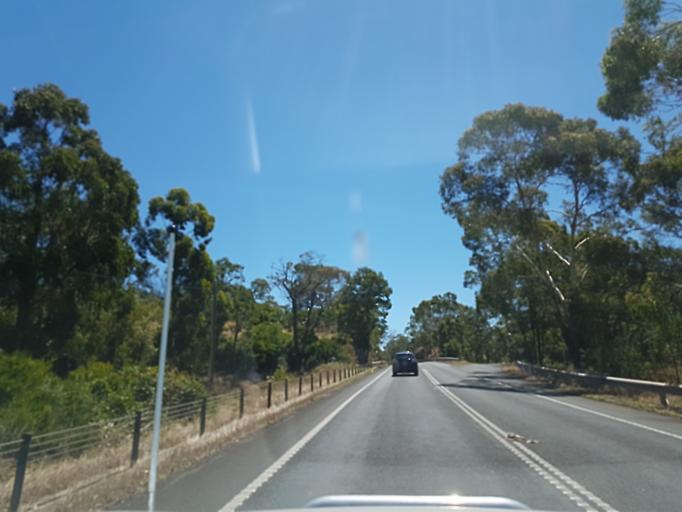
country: AU
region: Victoria
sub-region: Colac-Otway
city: Colac
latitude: -38.3482
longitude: 143.4146
